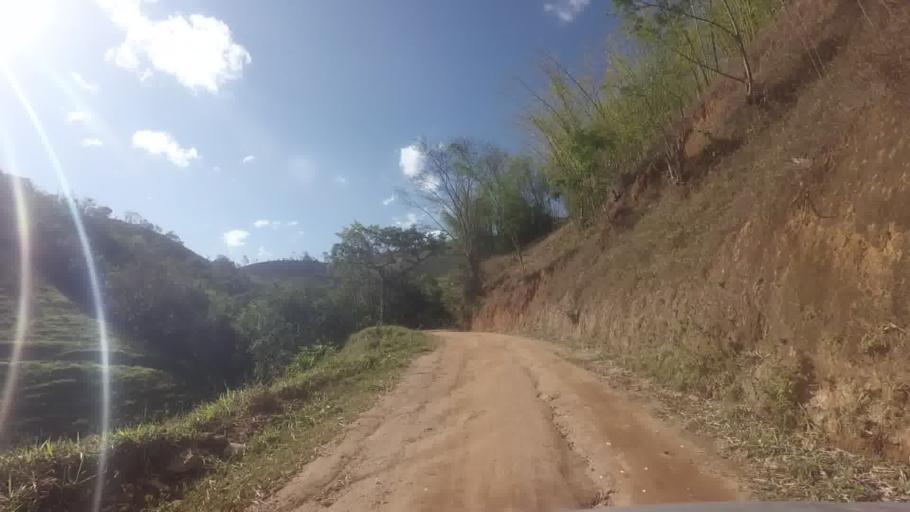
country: BR
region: Espirito Santo
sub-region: Sao Jose Do Calcado
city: Sao Jose do Calcado
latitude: -21.0372
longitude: -41.5997
